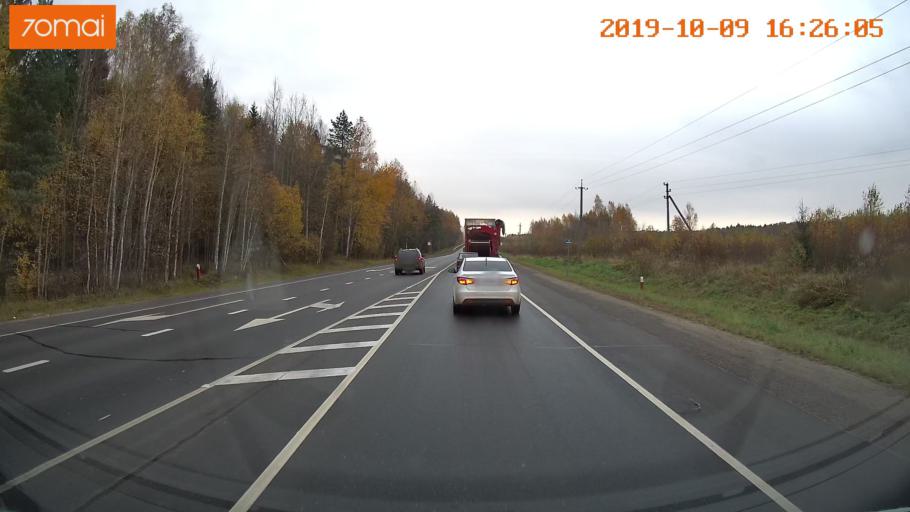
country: RU
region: Kostroma
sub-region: Kostromskoy Rayon
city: Kostroma
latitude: 57.6392
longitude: 40.9226
